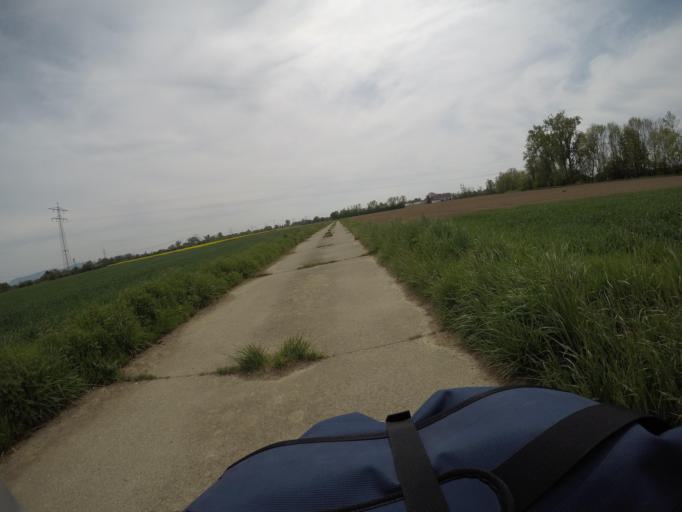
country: DE
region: Baden-Wuerttemberg
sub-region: Freiburg Region
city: Kehl
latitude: 48.5803
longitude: 7.8512
